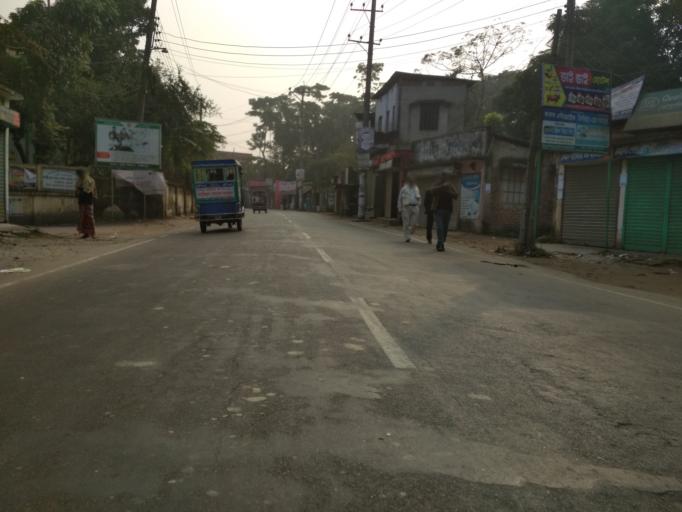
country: BD
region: Chittagong
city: Lakshmipur
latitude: 22.9412
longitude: 90.8415
